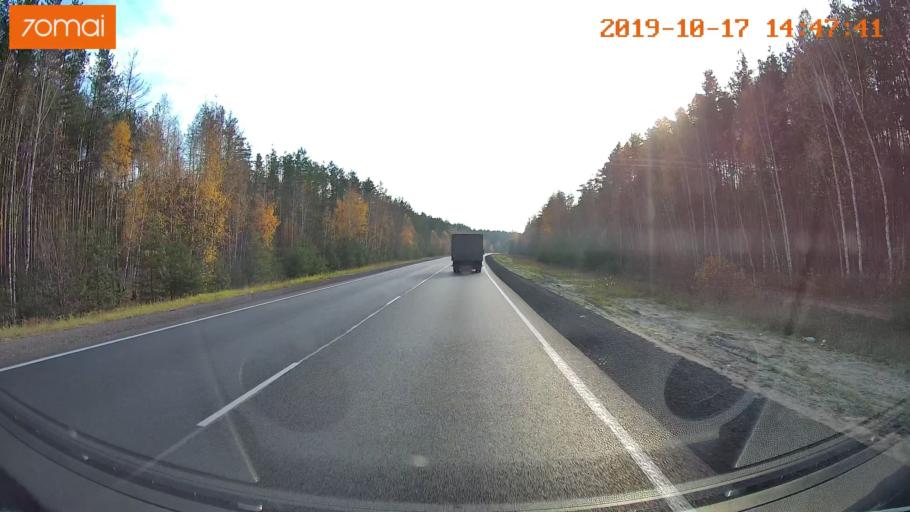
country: RU
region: Rjazan
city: Solotcha
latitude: 54.7679
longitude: 39.8583
